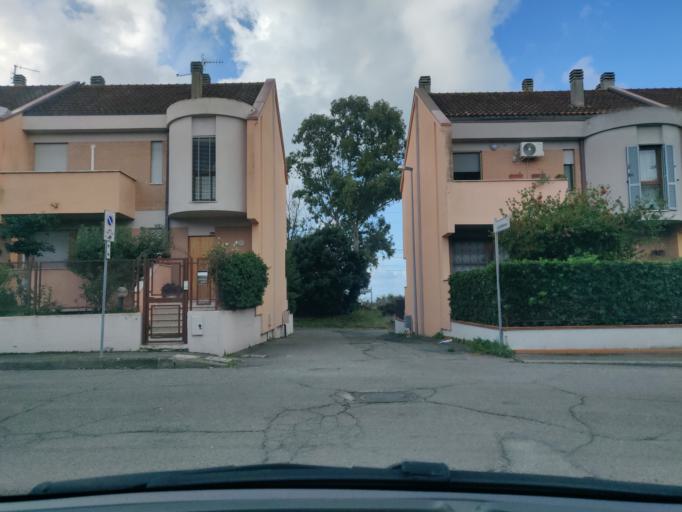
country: IT
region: Latium
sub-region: Citta metropolitana di Roma Capitale
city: Aurelia
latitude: 42.1361
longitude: 11.7840
